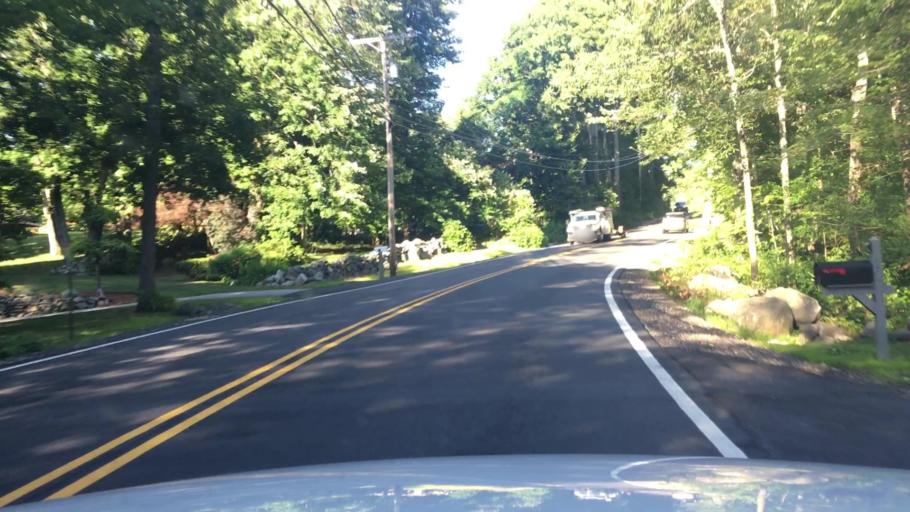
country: US
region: New Hampshire
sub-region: Rockingham County
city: Sandown
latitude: 42.9139
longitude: -71.1661
